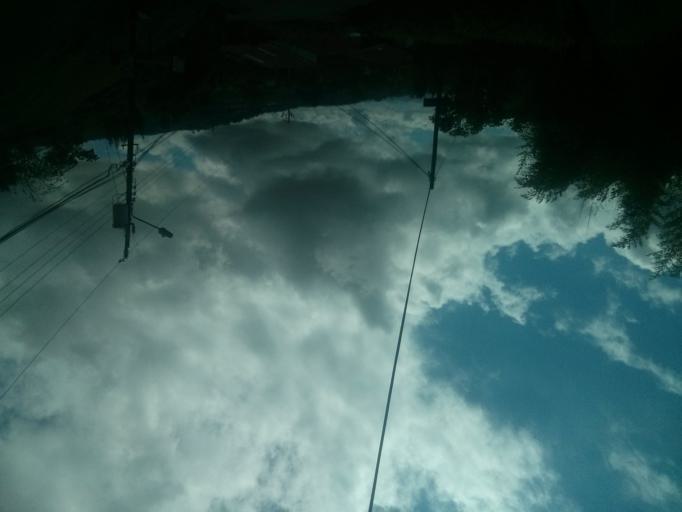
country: CR
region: Cartago
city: Cot
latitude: 9.9212
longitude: -83.7875
